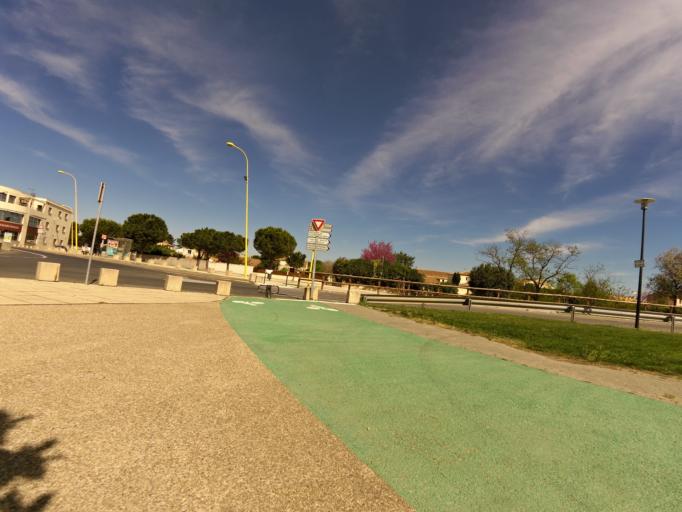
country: FR
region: Languedoc-Roussillon
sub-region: Departement de l'Herault
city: Lunel
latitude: 43.6680
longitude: 4.1273
